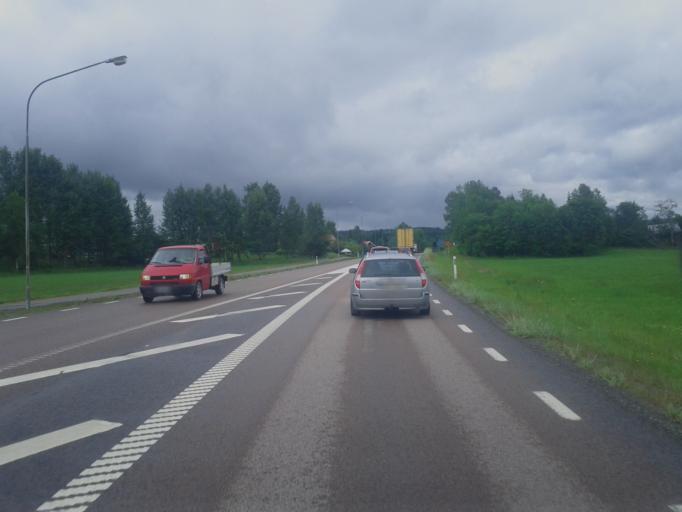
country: SE
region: Vaesternorrland
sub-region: Haernoesands Kommun
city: Haernoesand
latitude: 62.6688
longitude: 17.8411
